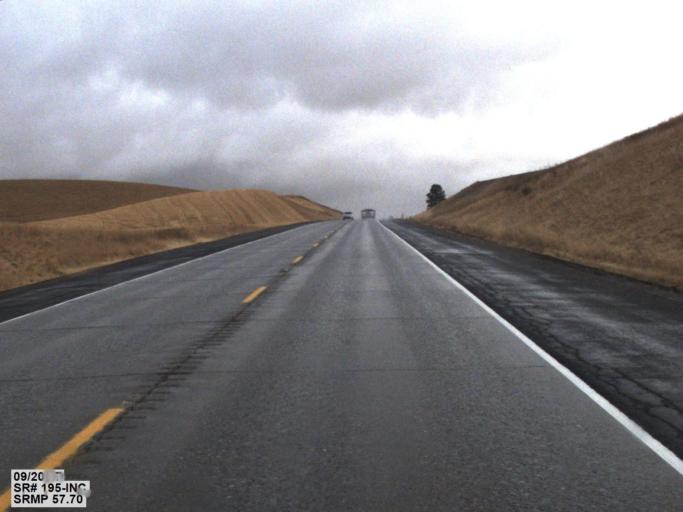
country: US
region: Washington
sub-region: Whitman County
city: Colfax
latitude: 47.1415
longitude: -117.3795
